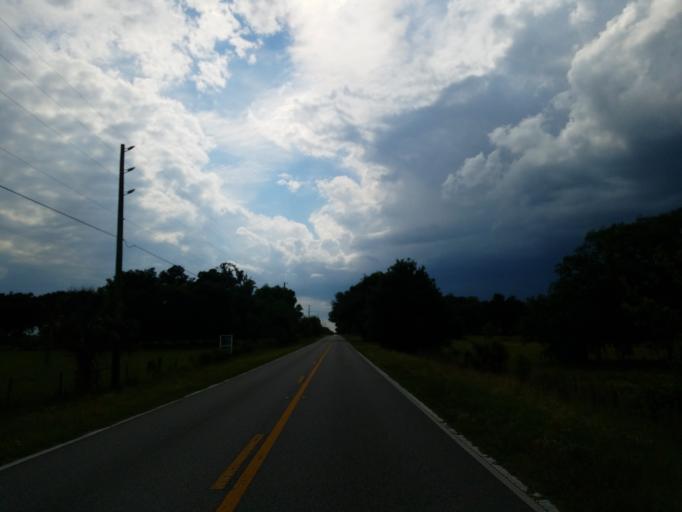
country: US
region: Florida
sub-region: Hernando County
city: Hill 'n Dale
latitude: 28.5533
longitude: -82.3319
